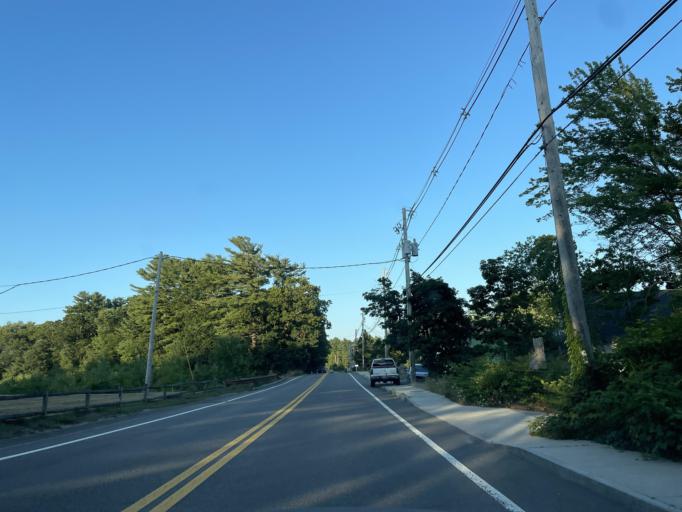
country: US
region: Massachusetts
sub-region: Plymouth County
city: North Pembroke
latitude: 42.0612
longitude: -70.8271
